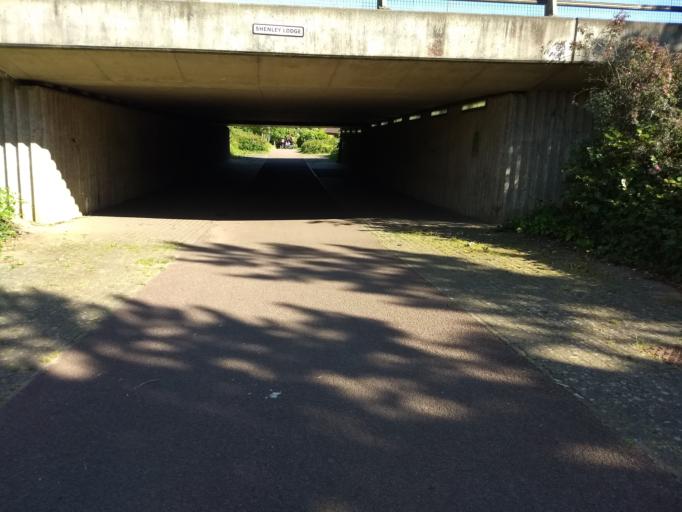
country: GB
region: England
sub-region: Milton Keynes
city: Shenley Church End
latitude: 52.0205
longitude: -0.7803
